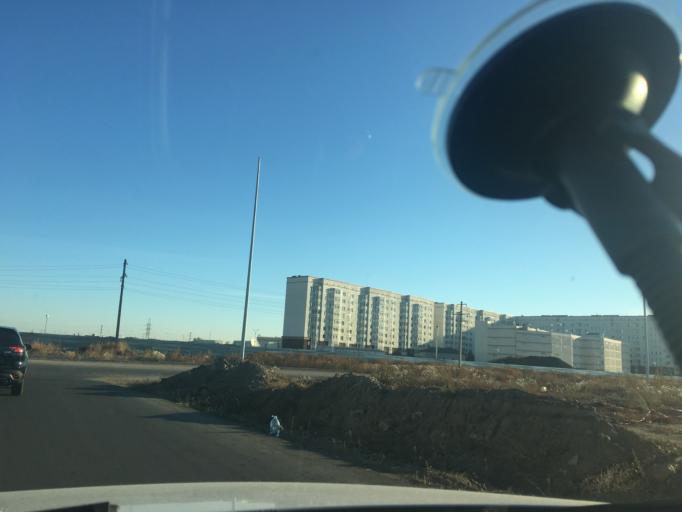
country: KZ
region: Astana Qalasy
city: Astana
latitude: 51.1425
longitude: 71.3714
